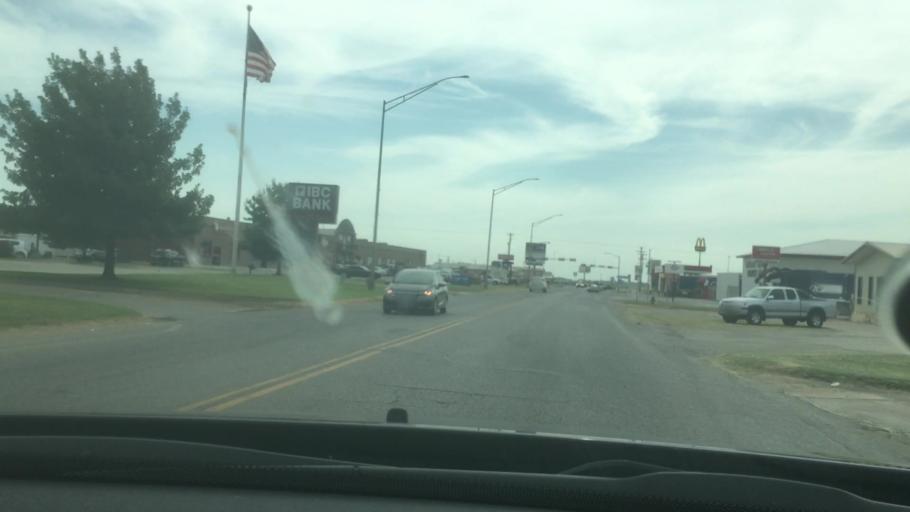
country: US
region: Oklahoma
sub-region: Garvin County
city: Lindsay
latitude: 34.8368
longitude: -97.6009
